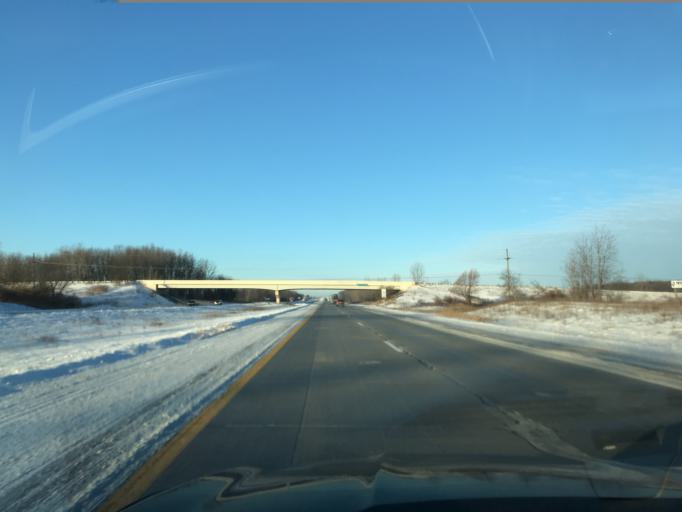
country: US
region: Michigan
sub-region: Lapeer County
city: Imlay City
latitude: 42.9996
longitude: -83.0834
